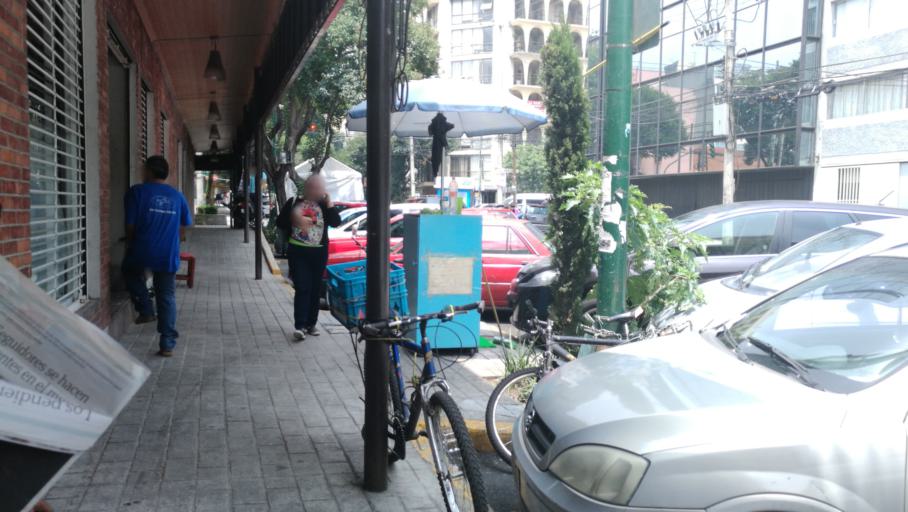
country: MX
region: Mexico City
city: Colonia del Valle
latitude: 19.3772
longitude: -99.1740
